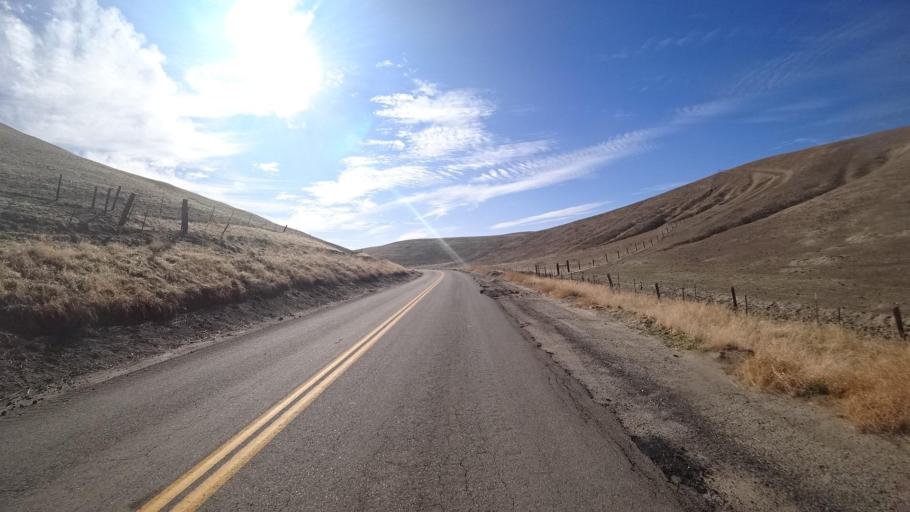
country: US
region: California
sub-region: Kern County
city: Oildale
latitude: 35.6170
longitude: -118.9427
